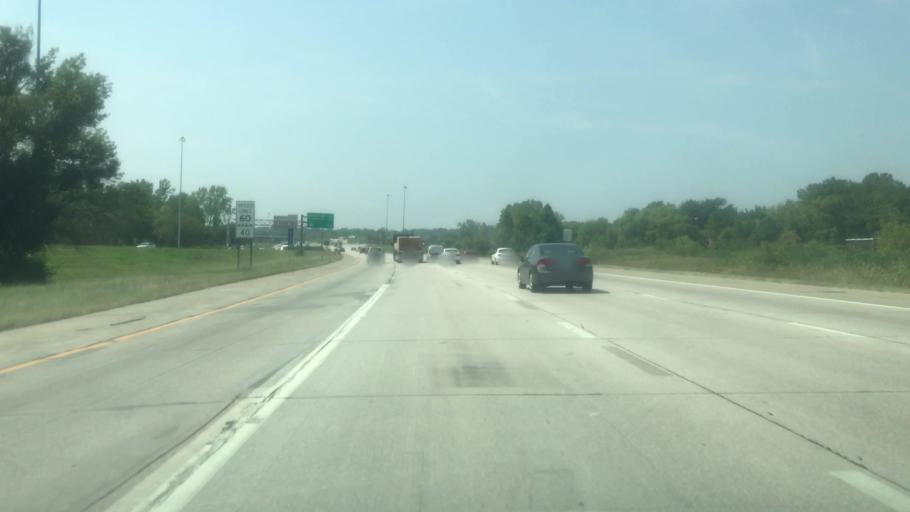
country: US
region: Kansas
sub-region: Johnson County
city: Merriam
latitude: 39.0395
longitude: -94.6786
